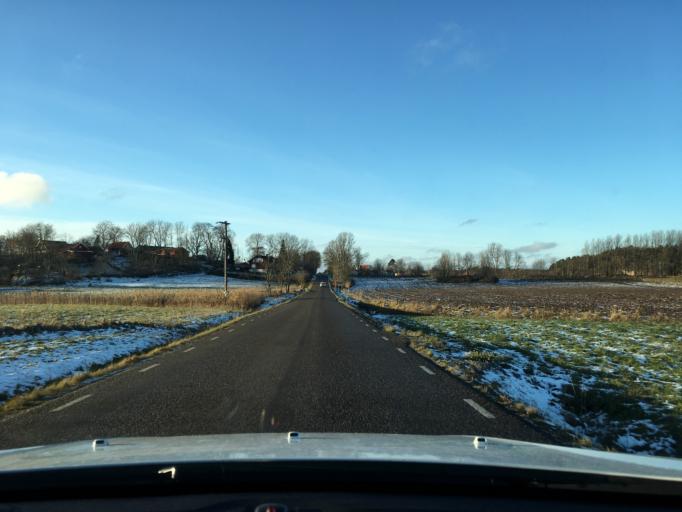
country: SE
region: Vaestra Goetaland
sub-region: Tjorns Kommun
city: Myggenas
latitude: 58.0486
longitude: 11.7182
